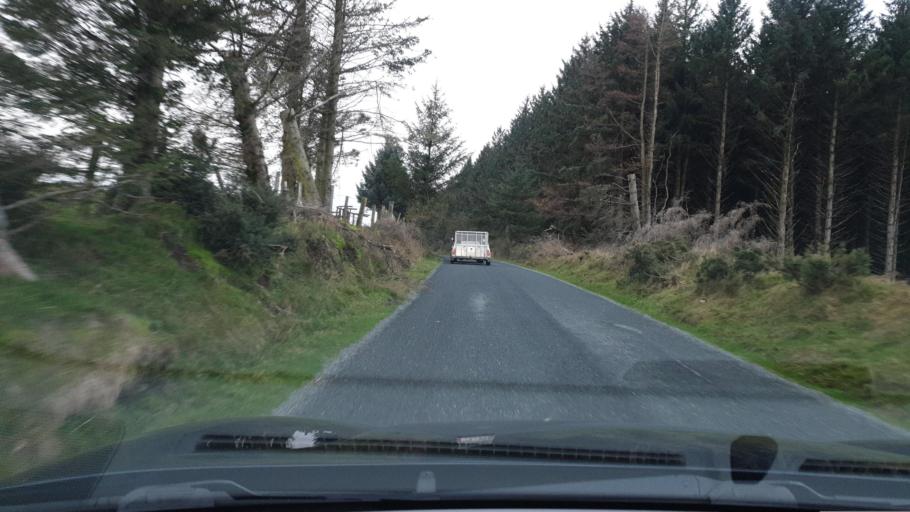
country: IE
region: Leinster
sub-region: Wicklow
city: Enniskerry
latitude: 53.1510
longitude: -6.1880
